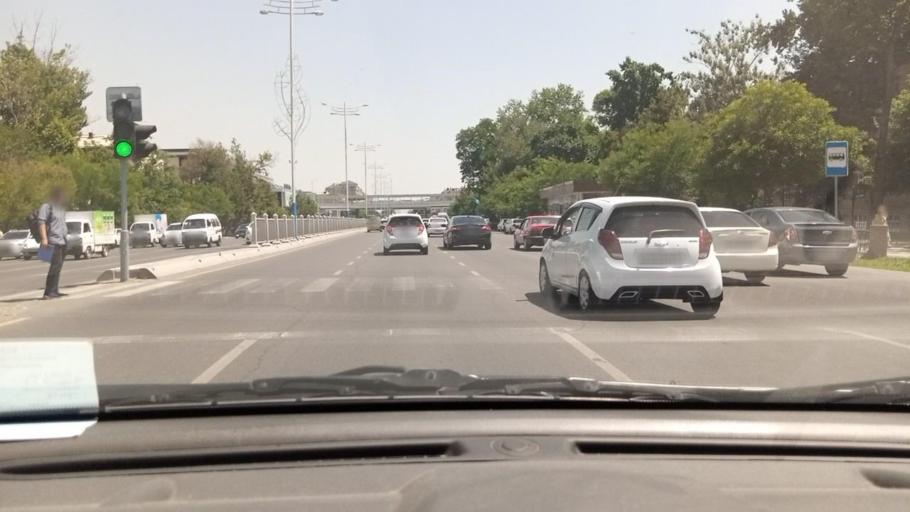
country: UZ
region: Toshkent Shahri
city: Tashkent
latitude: 41.2939
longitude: 69.2203
